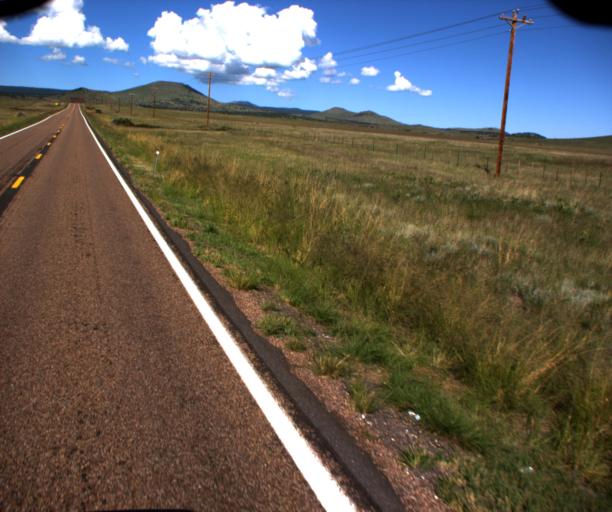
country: US
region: Arizona
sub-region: Apache County
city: Eagar
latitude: 34.0996
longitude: -109.3912
